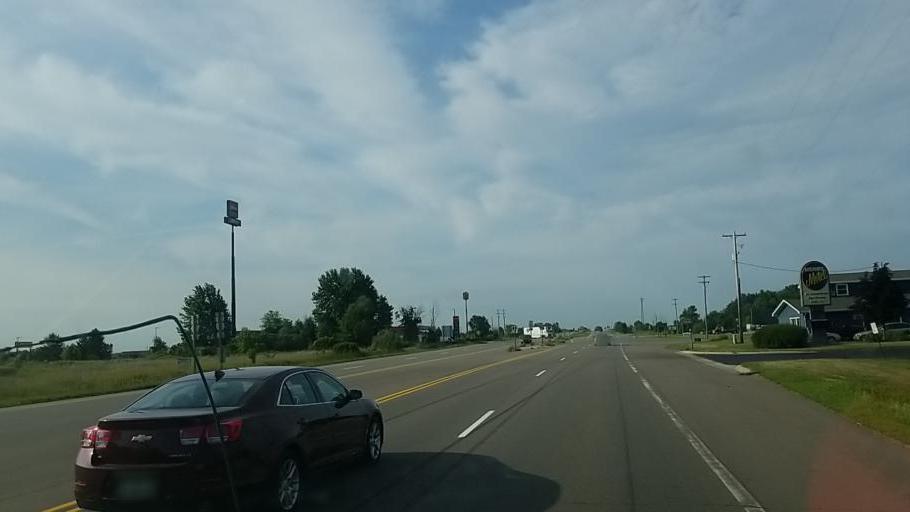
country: US
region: Michigan
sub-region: Ionia County
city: Ionia
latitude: 42.8852
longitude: -85.0751
